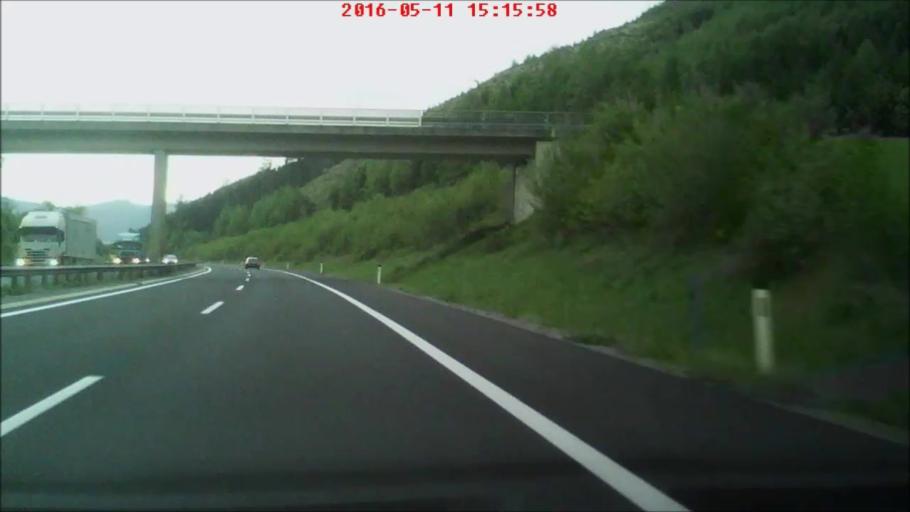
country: AT
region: Styria
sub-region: Politischer Bezirk Leoben
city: Kammern im Liesingtal
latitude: 47.3855
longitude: 14.9196
